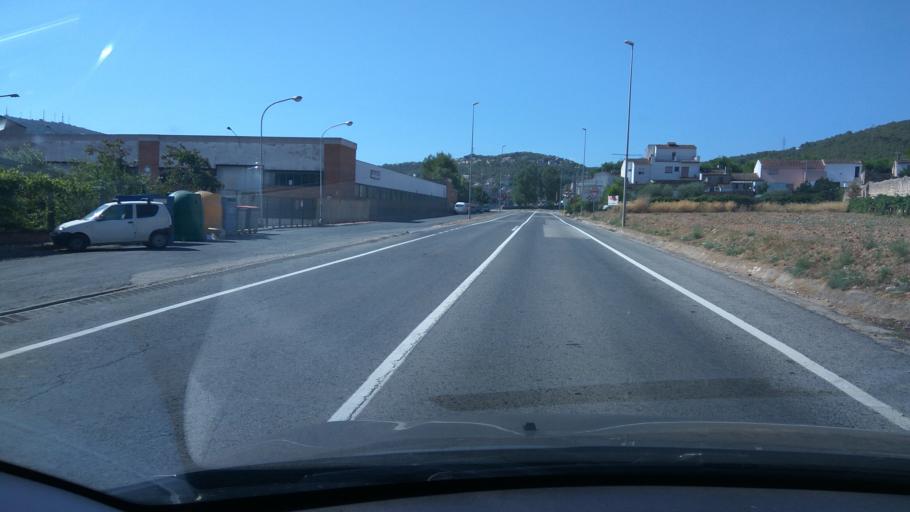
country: ES
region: Catalonia
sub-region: Provincia de Barcelona
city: Sant Pere de Ribes
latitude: 41.2868
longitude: 1.7239
